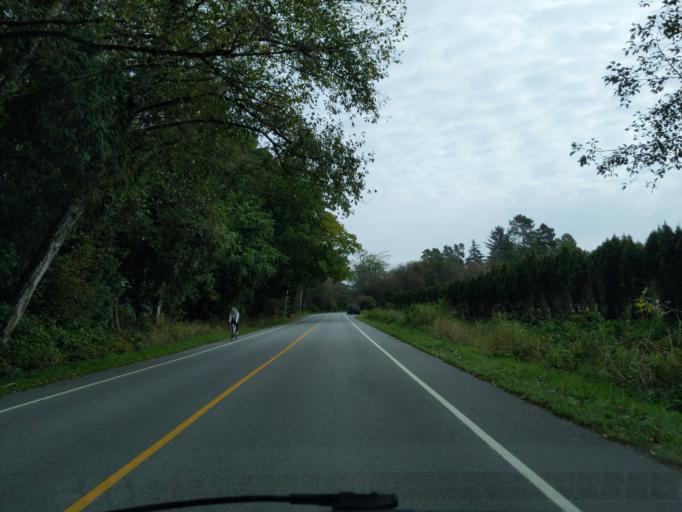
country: CA
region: British Columbia
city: Maple Ridge
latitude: 49.2060
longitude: -122.6067
